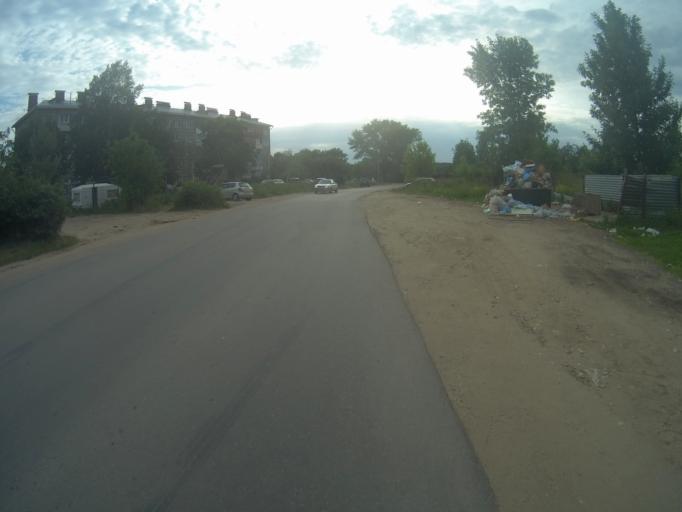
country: RU
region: Vladimir
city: Vladimir
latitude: 56.2204
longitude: 40.4097
